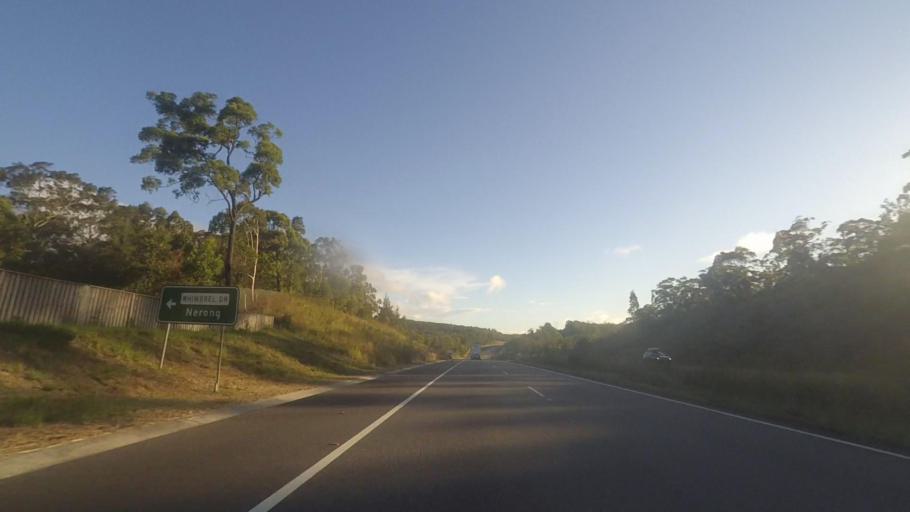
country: AU
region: New South Wales
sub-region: Great Lakes
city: Bulahdelah
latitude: -32.5082
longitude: 152.2111
